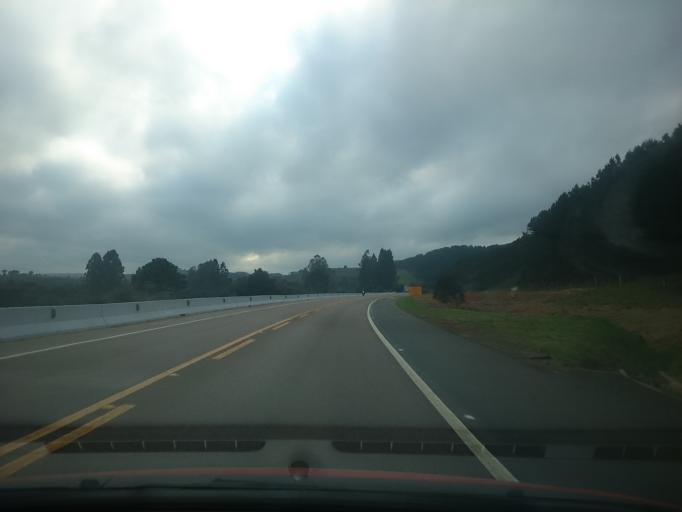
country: BR
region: Santa Catarina
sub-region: Lages
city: Lages
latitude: -27.9086
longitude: -50.4453
